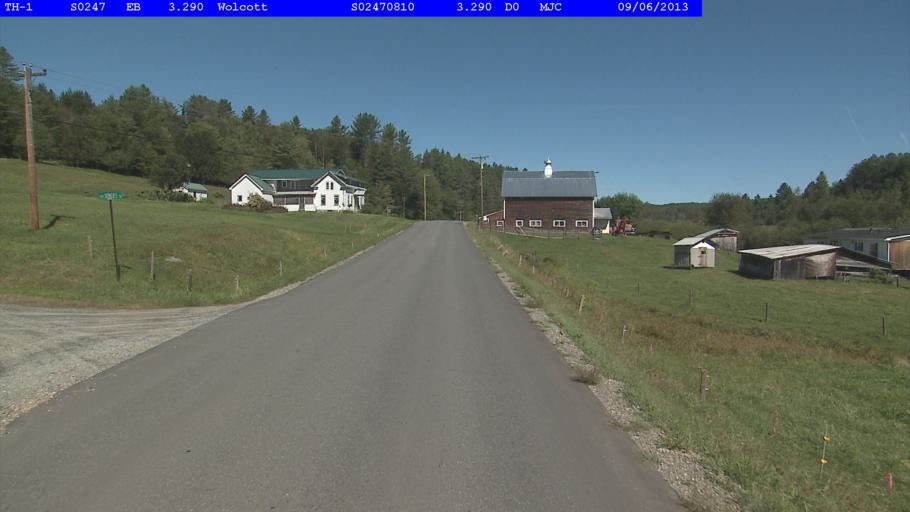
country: US
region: Vermont
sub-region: Caledonia County
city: Hardwick
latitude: 44.6009
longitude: -72.4663
